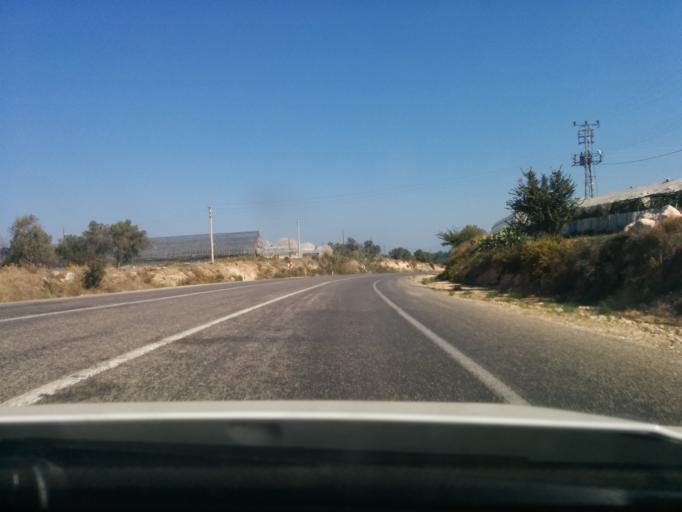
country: TR
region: Mugla
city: Esen
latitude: 36.3832
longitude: 29.3222
